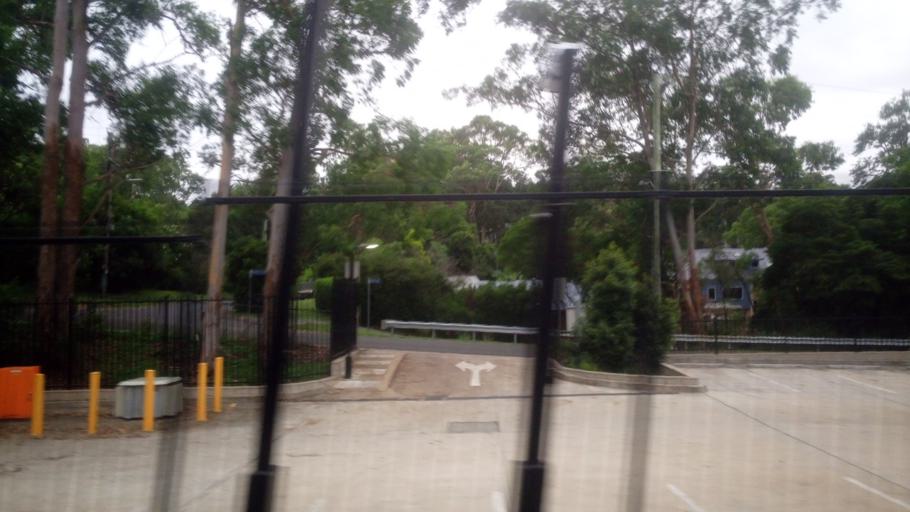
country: AU
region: New South Wales
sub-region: Blue Mountains Municipality
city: Glenbrook
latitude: -33.7686
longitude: 150.6190
